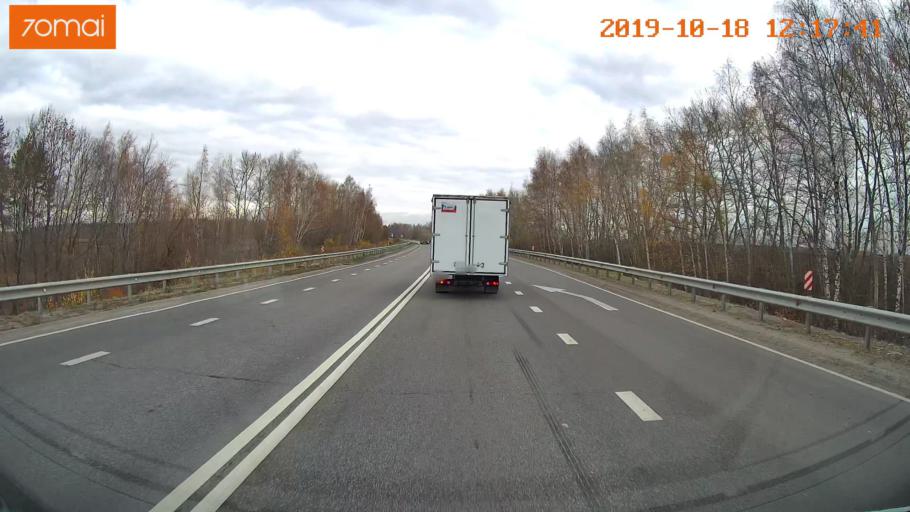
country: RU
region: Rjazan
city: Zakharovo
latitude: 54.4592
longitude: 39.4478
